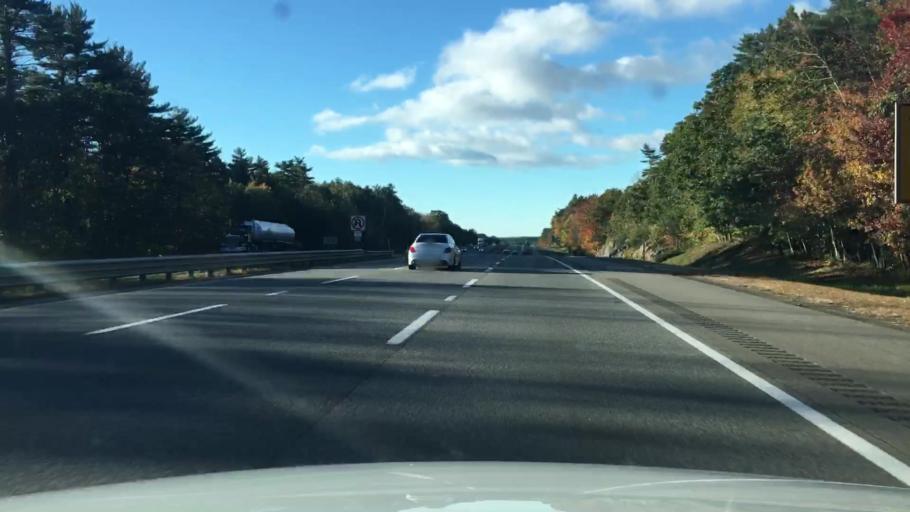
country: US
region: Maine
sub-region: York County
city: Cape Neddick
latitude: 43.1801
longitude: -70.6489
